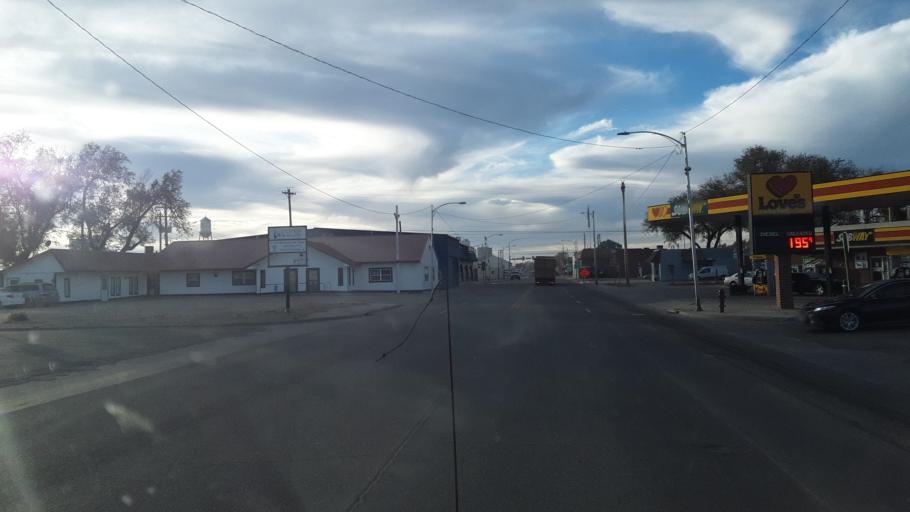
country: US
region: Kansas
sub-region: Hamilton County
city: Syracuse
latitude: 37.9799
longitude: -101.7499
